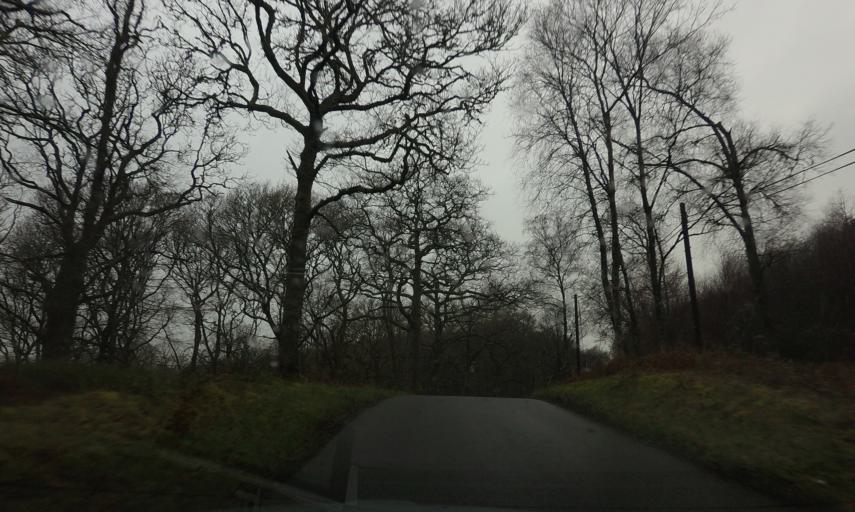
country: GB
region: Scotland
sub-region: West Dunbartonshire
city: Balloch
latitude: 56.1217
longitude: -4.5936
